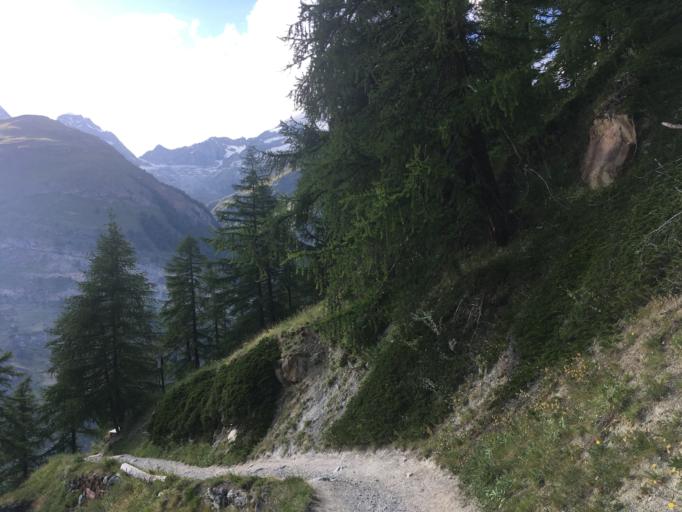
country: CH
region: Valais
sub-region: Visp District
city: Zermatt
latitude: 46.0112
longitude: 7.7530
